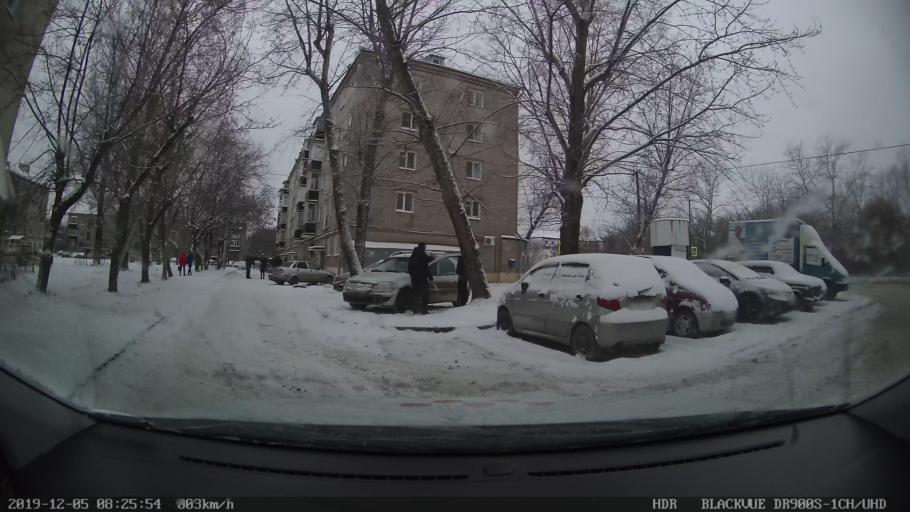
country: RU
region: Tatarstan
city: Staroye Arakchino
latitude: 55.8786
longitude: 49.0239
